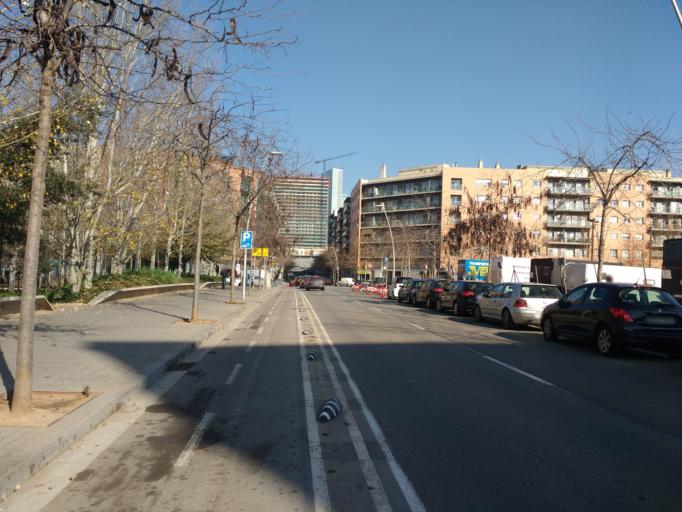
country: ES
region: Catalonia
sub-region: Provincia de Barcelona
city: Sant Marti
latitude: 41.4027
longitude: 2.1954
